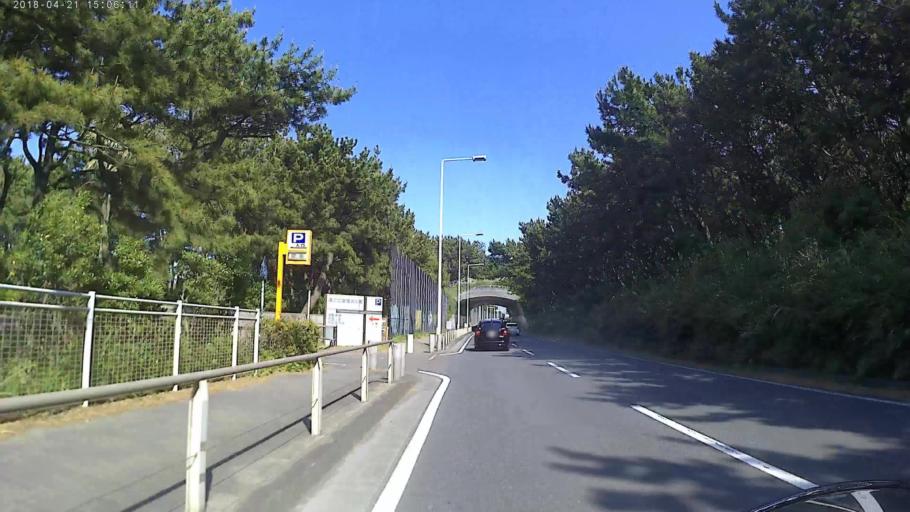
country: JP
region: Kanagawa
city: Fujisawa
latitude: 35.3205
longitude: 139.4457
